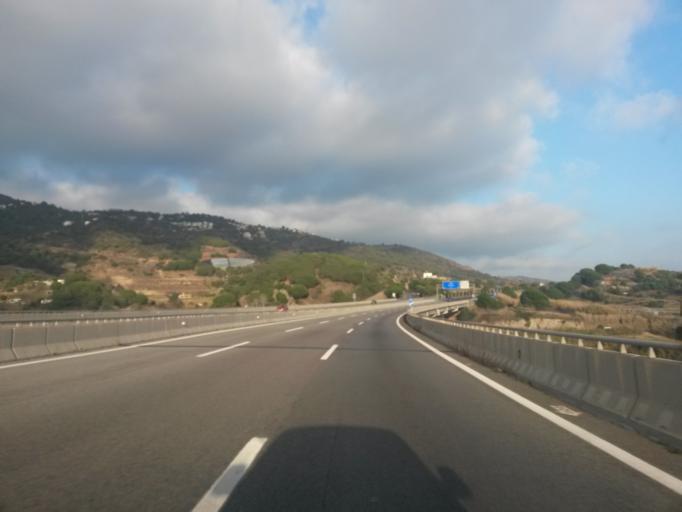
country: ES
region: Catalonia
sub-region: Provincia de Barcelona
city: Calella
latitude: 41.6242
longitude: 2.6495
